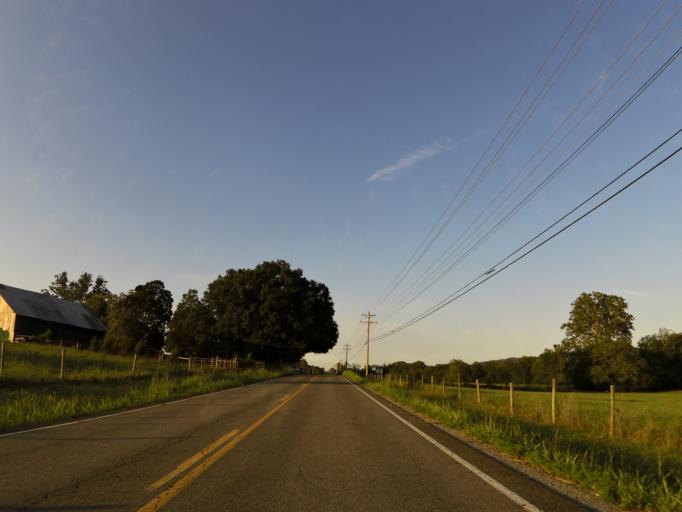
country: US
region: Tennessee
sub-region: Roane County
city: Rockwood
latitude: 35.6981
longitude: -84.6549
